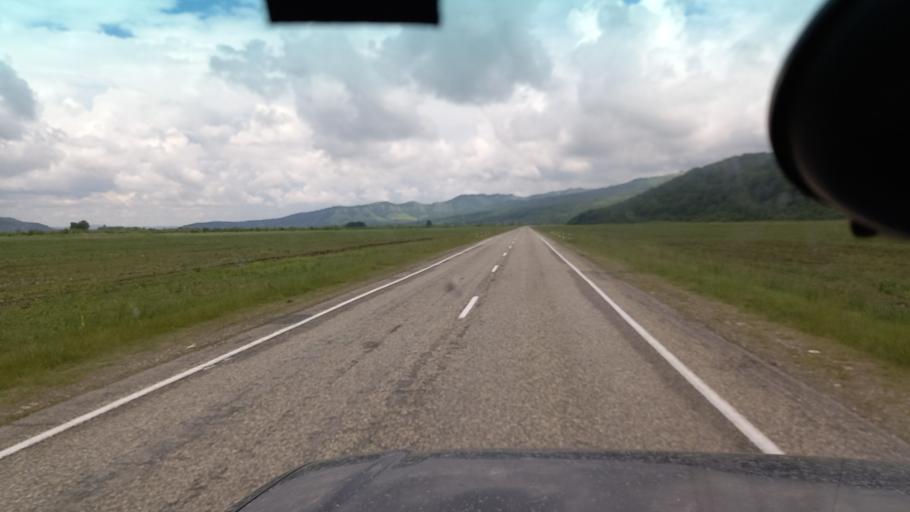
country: RU
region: Krasnodarskiy
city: Psebay
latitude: 44.0964
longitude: 40.8109
